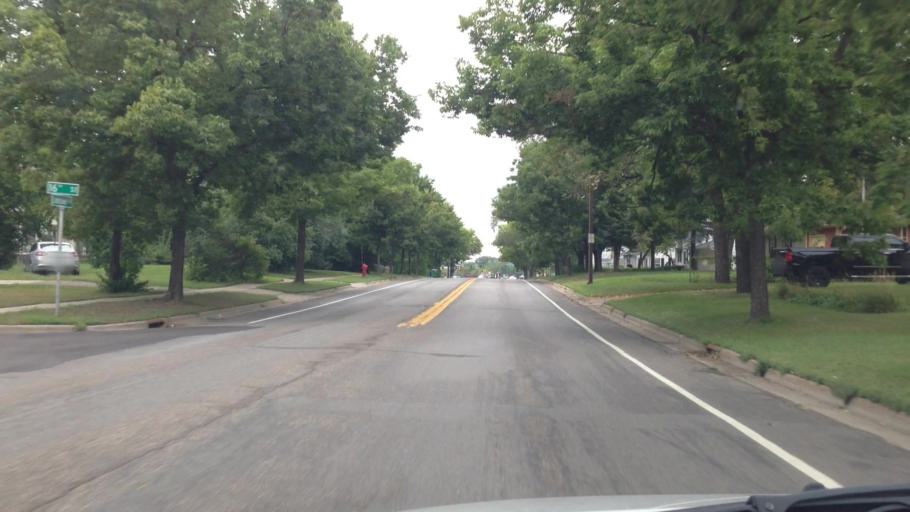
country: US
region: Minnesota
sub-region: Hennepin County
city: Saint Louis Park
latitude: 44.9674
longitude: -93.3708
